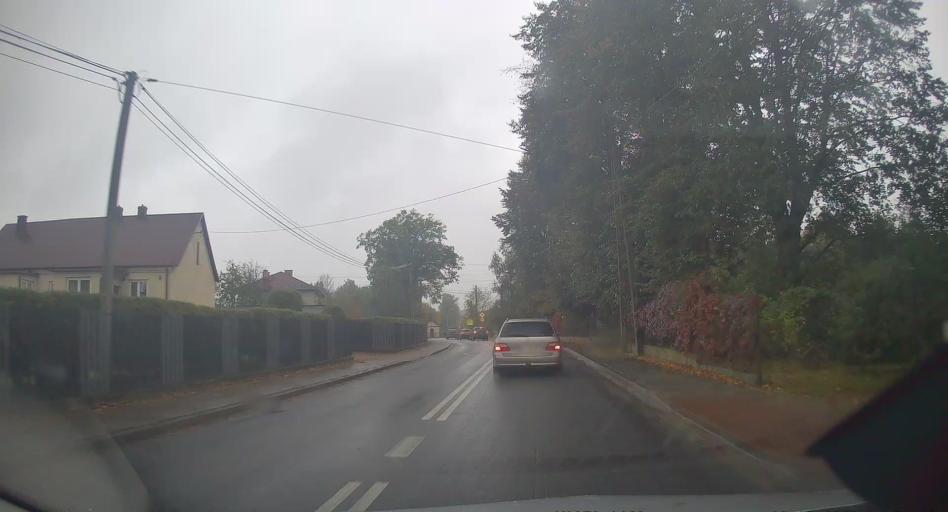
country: PL
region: Lesser Poland Voivodeship
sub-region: Powiat krakowski
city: Ochojno
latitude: 49.9813
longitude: 19.9896
